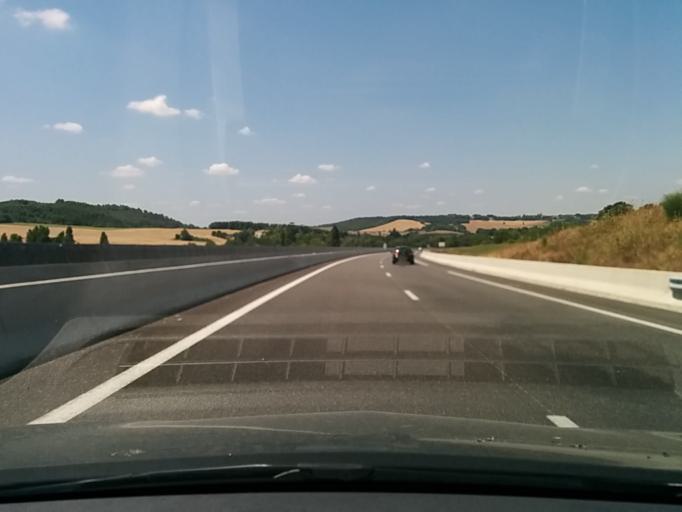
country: FR
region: Midi-Pyrenees
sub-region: Departement du Gers
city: Preignan
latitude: 43.6526
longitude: 0.6700
